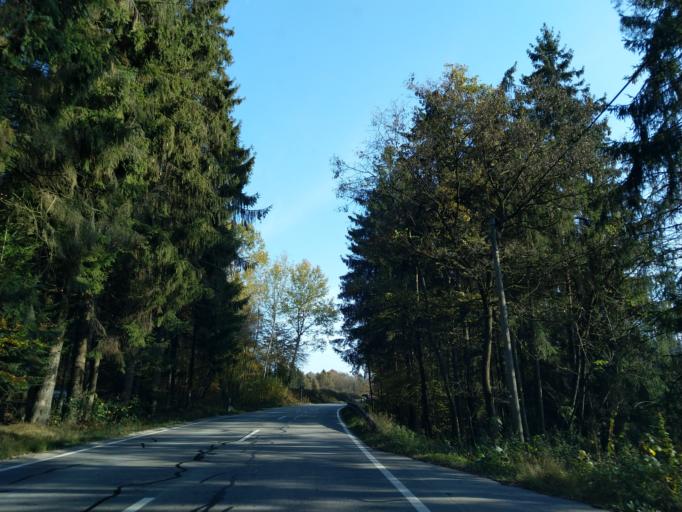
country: DE
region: Bavaria
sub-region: Lower Bavaria
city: Auerbach
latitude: 48.8088
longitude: 13.1104
